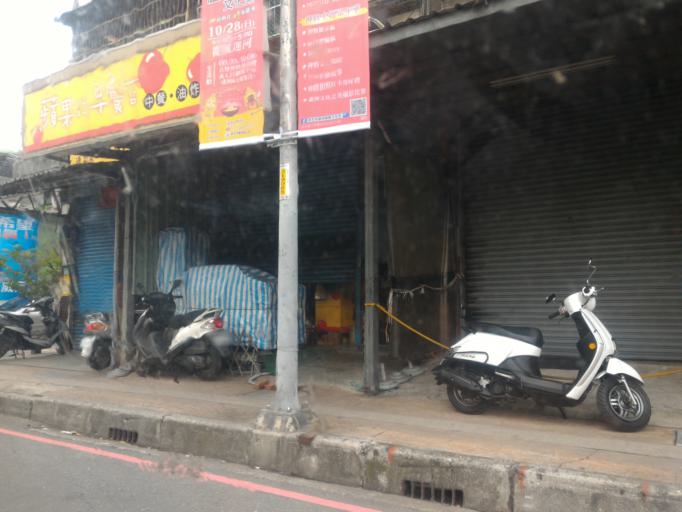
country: TW
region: Taipei
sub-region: Taipei
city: Banqiao
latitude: 25.0895
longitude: 121.4656
